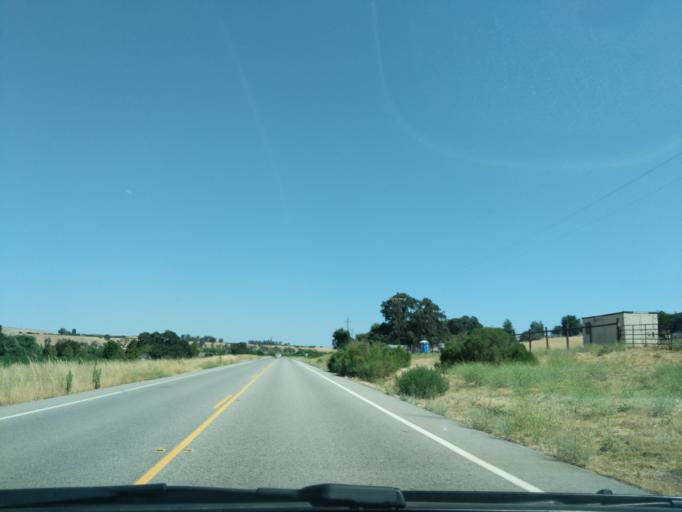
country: US
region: California
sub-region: San Luis Obispo County
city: San Miguel
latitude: 35.7666
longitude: -120.6992
